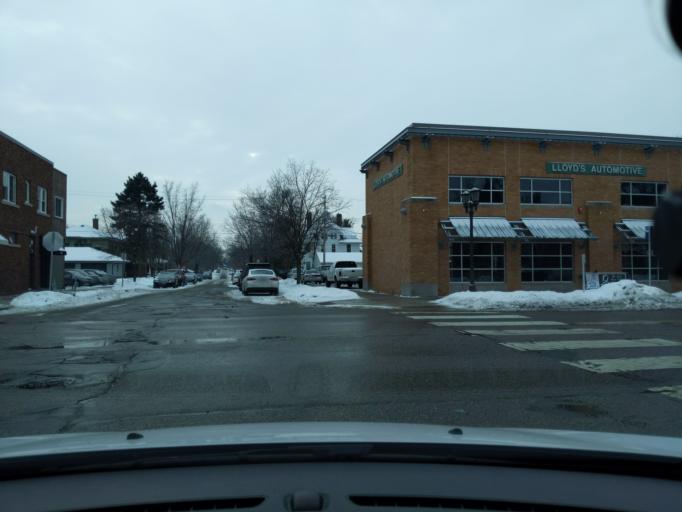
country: US
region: Minnesota
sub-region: Dakota County
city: West Saint Paul
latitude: 44.9401
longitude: -93.1416
